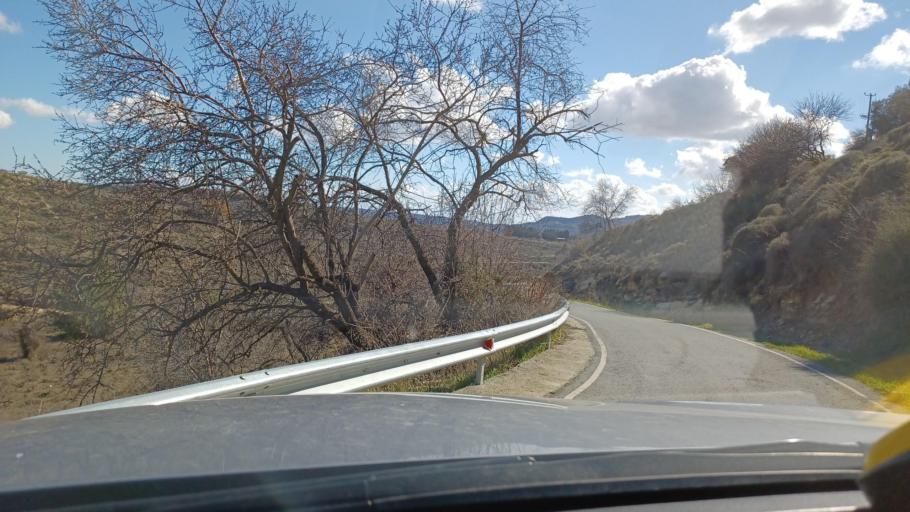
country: CY
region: Limassol
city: Pachna
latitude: 34.8260
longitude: 32.7802
